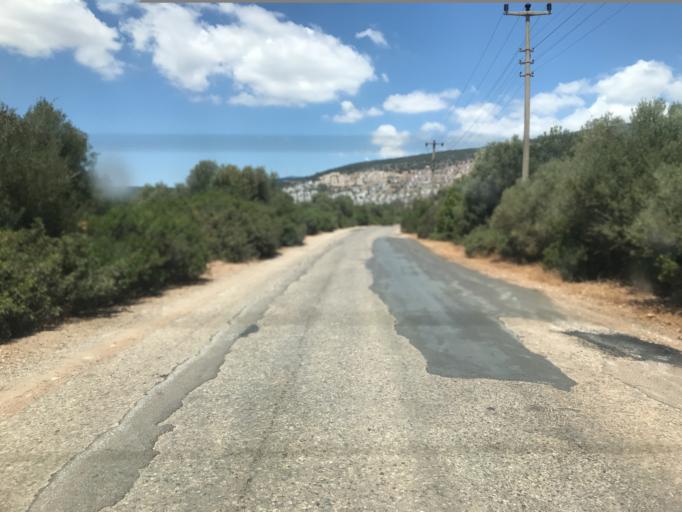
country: TR
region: Aydin
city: Sarikemer
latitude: 37.4108
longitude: 27.4231
